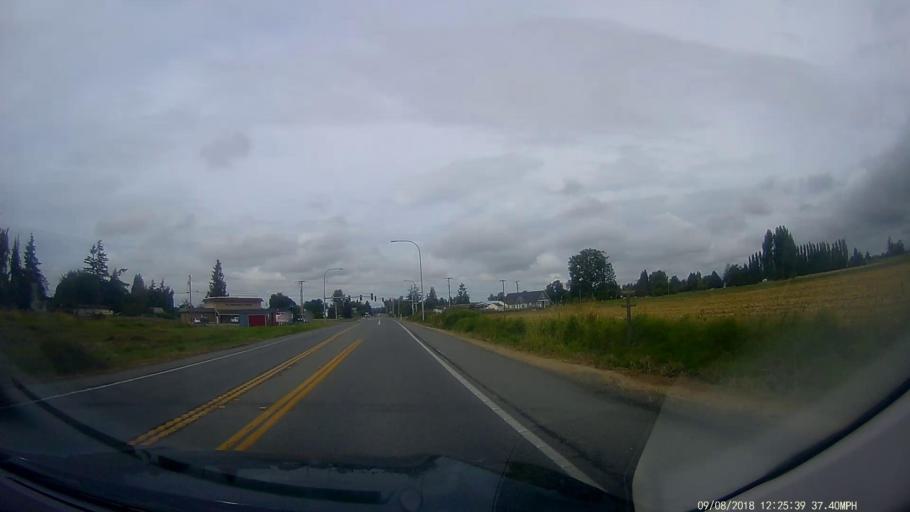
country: US
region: Washington
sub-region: Skagit County
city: Mount Vernon
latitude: 48.4353
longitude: -122.3766
